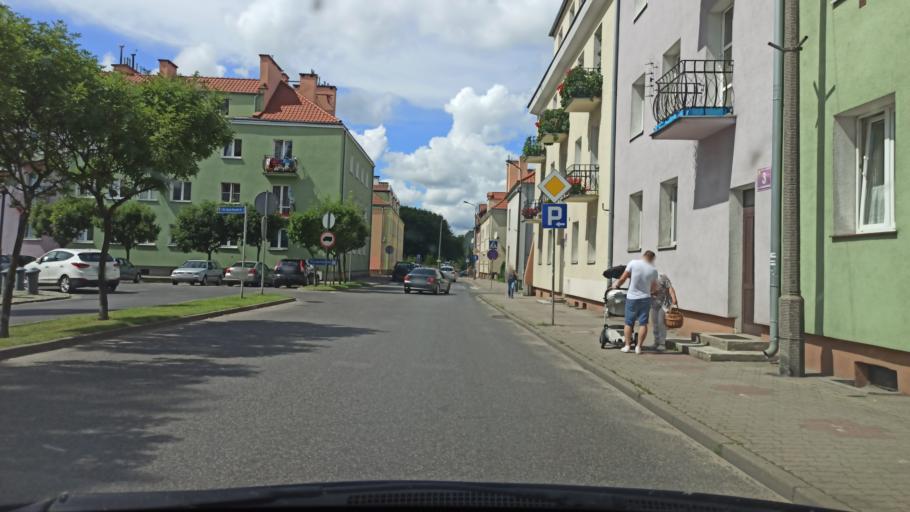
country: PL
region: Warmian-Masurian Voivodeship
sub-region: Powiat ostrodzki
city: Morag
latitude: 53.9119
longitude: 19.9286
